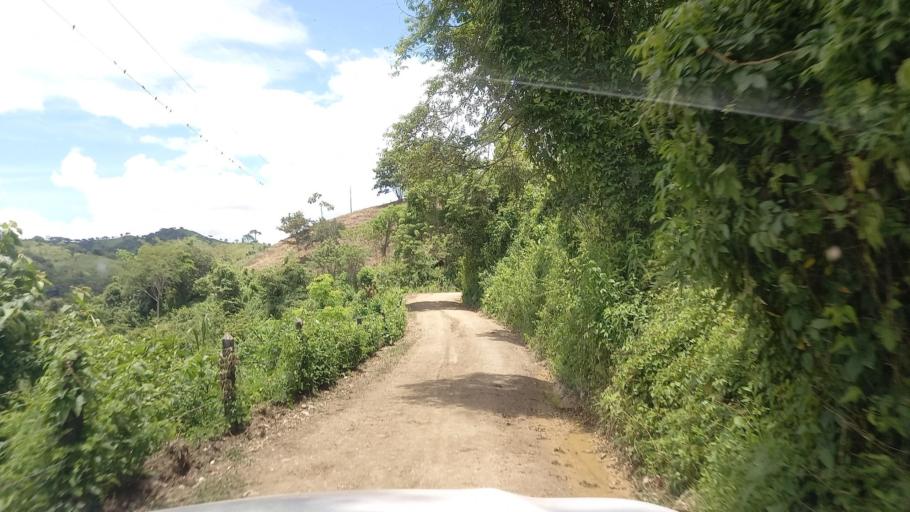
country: NI
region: Nueva Segovia
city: Wiwili
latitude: 13.7379
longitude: -85.7886
